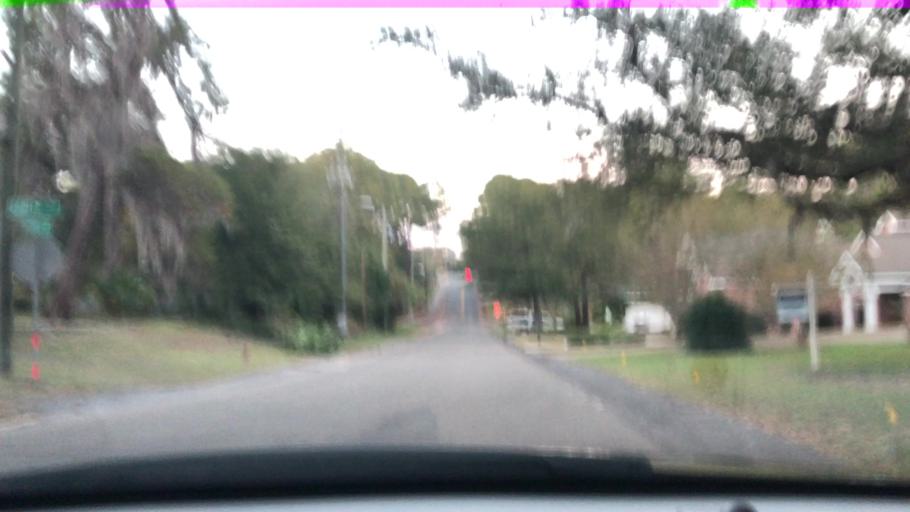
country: US
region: Florida
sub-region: Bay County
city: Panama City
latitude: 30.1439
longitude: -85.6447
